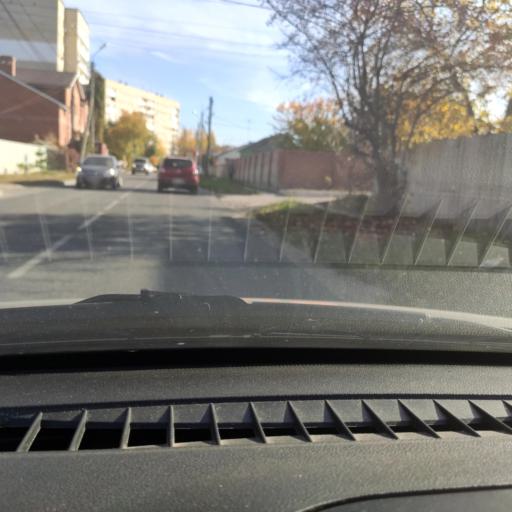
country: RU
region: Samara
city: Tol'yatti
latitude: 53.5085
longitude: 49.3973
